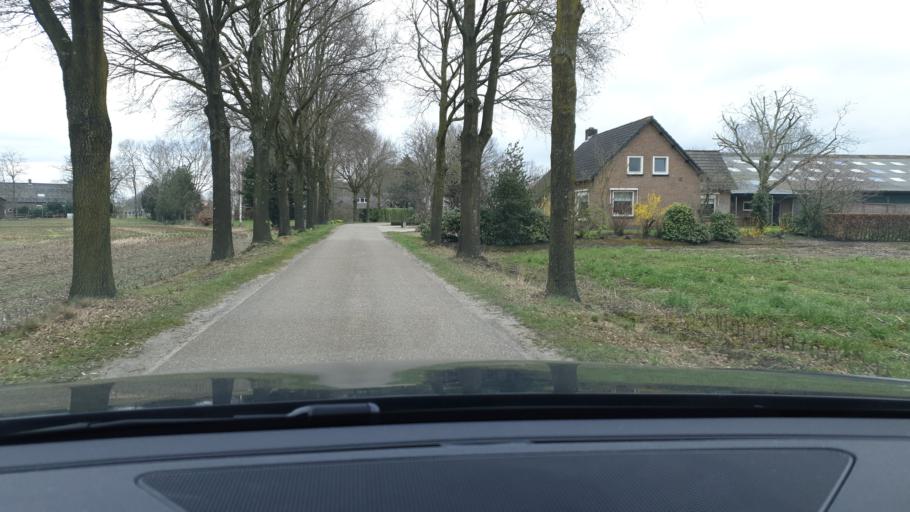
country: NL
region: North Brabant
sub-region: Gemeente Veldhoven
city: Oerle
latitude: 51.4286
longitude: 5.3359
